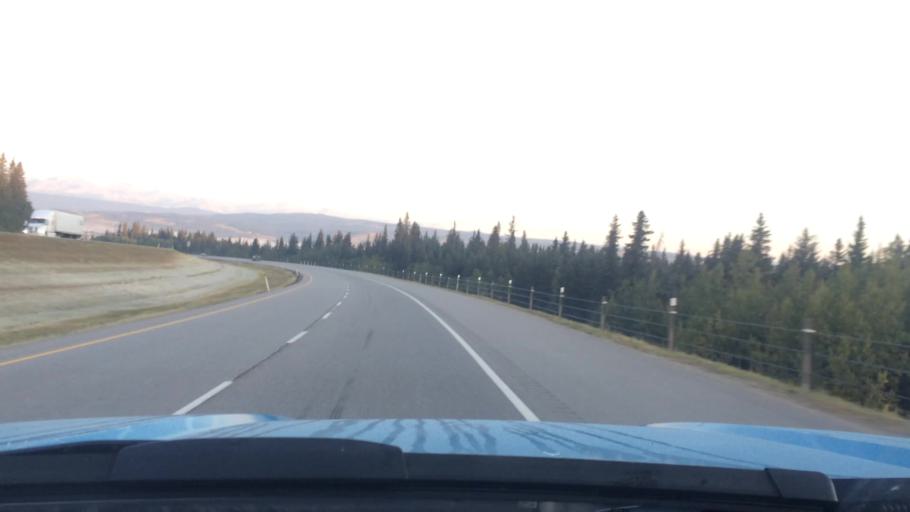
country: CA
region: Alberta
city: Cochrane
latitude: 51.1605
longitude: -114.7551
